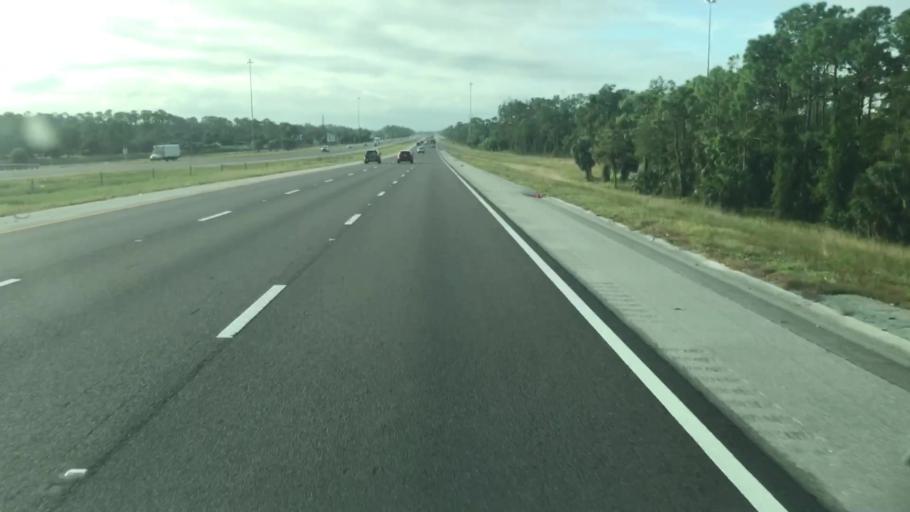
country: US
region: Florida
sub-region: Collier County
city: Vineyards
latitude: 26.2097
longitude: -81.7365
